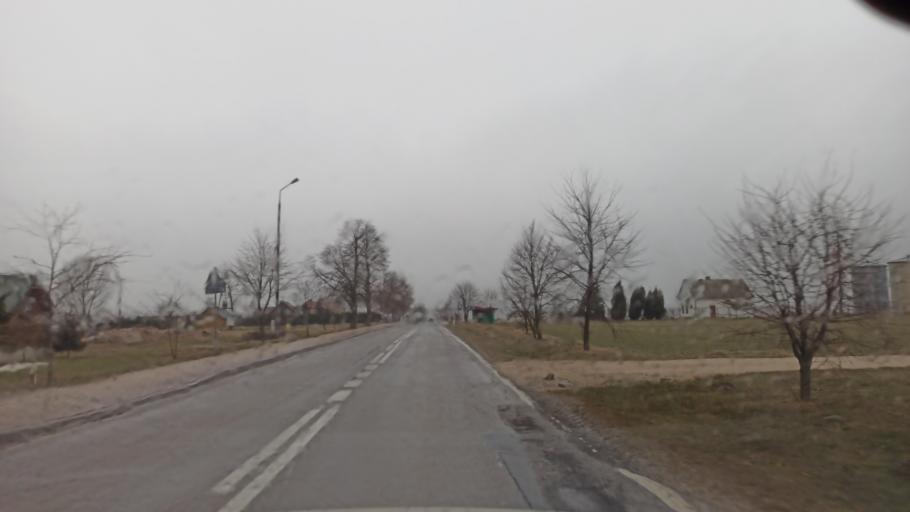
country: PL
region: Lublin Voivodeship
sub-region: Powiat lubelski
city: Strzyzowice
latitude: 51.0433
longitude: 22.4645
